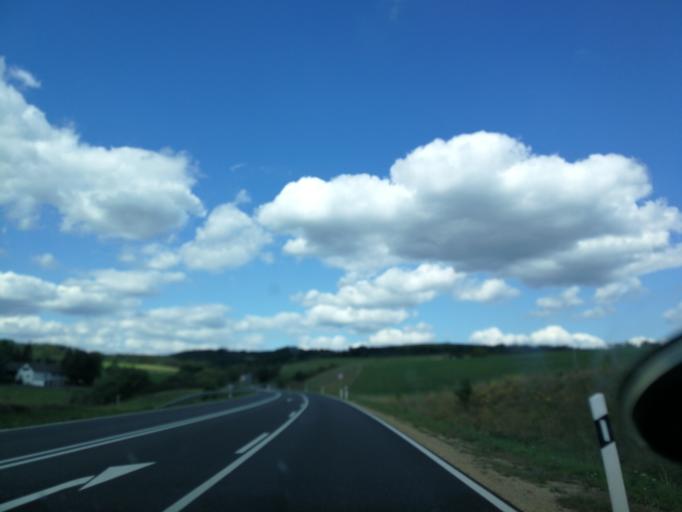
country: DE
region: Rheinland-Pfalz
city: Ohlenhard
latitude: 50.4108
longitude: 6.7383
